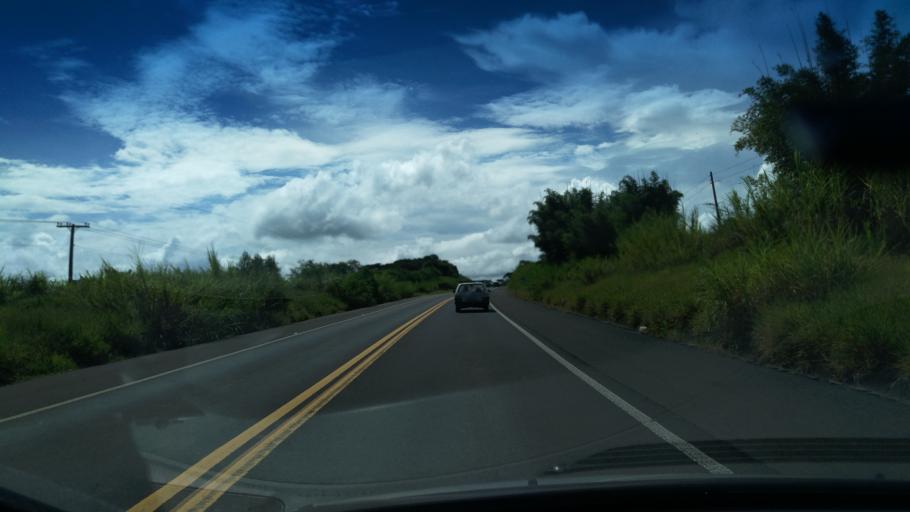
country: BR
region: Sao Paulo
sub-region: Santo Antonio Do Jardim
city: Espirito Santo do Pinhal
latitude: -22.1626
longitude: -46.7337
